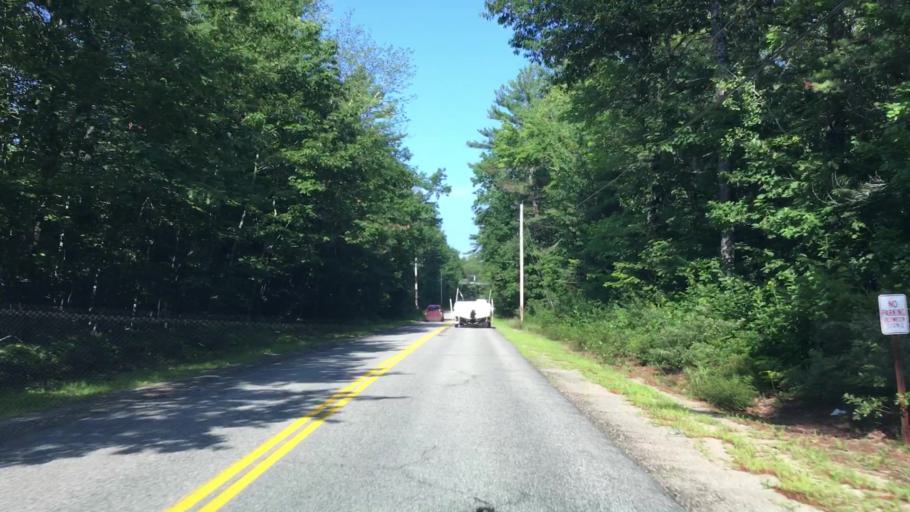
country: US
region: Maine
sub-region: Androscoggin County
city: Poland
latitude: 44.0428
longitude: -70.3486
